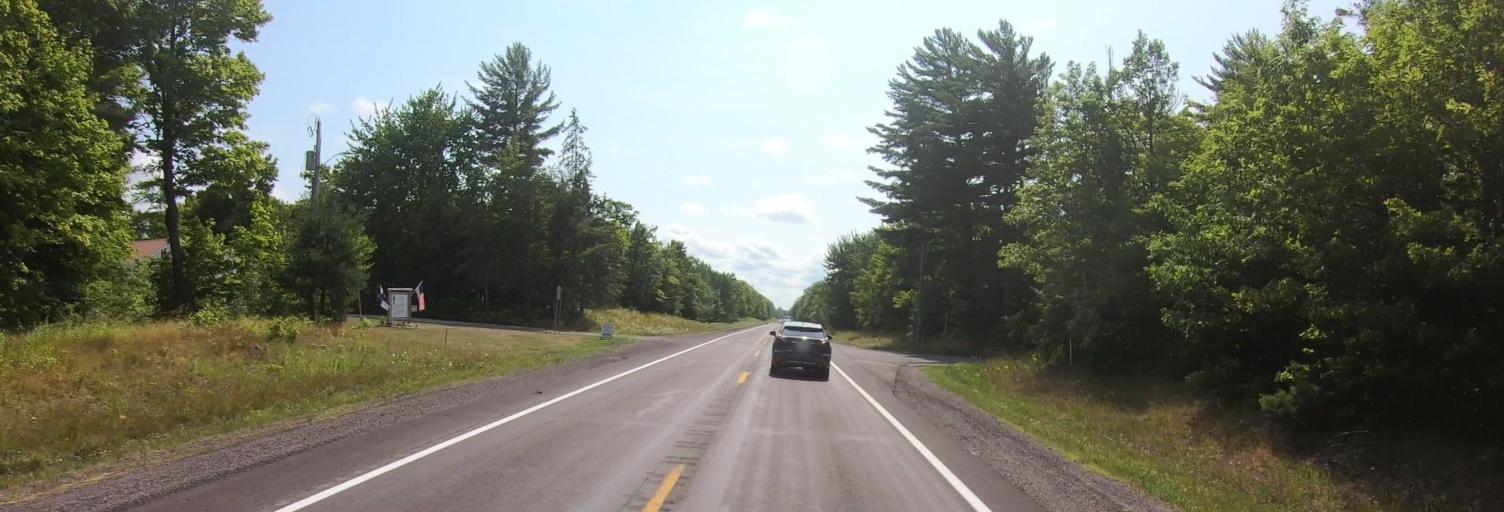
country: US
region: Michigan
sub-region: Houghton County
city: Hancock
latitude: 46.8683
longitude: -88.8994
